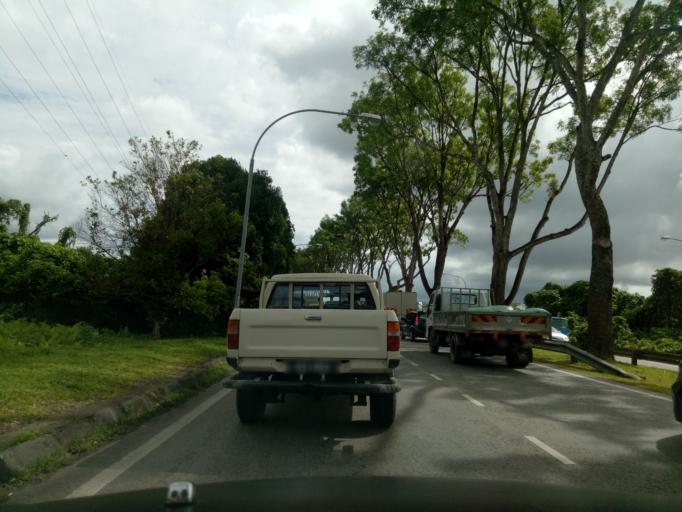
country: MY
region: Sarawak
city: Kuching
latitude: 1.5448
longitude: 110.3747
